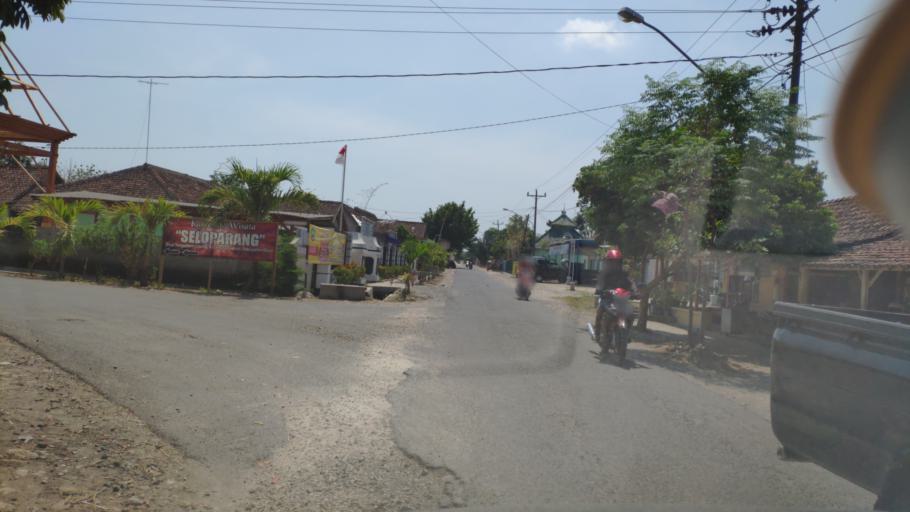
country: ID
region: Central Java
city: Tempel
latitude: -6.9777
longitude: 111.4965
